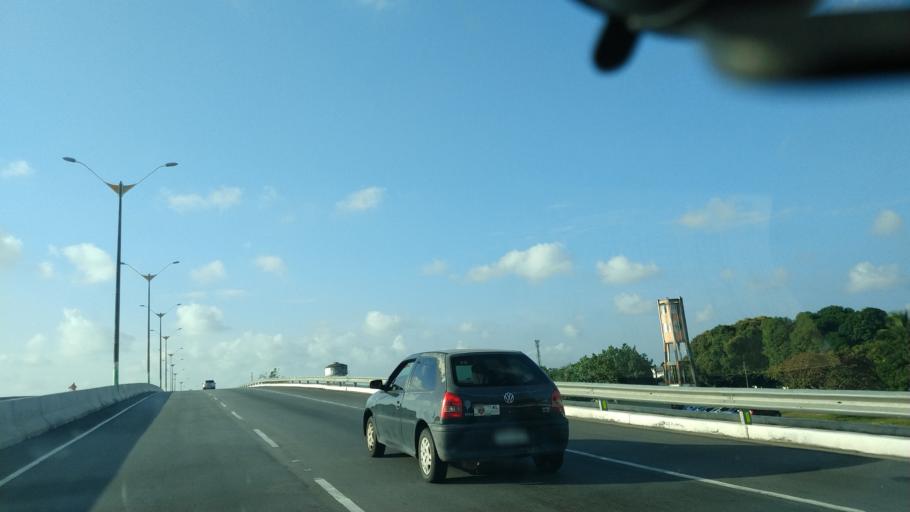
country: BR
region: Rio Grande do Norte
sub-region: Parnamirim
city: Parnamirim
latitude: -5.9240
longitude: -35.2647
